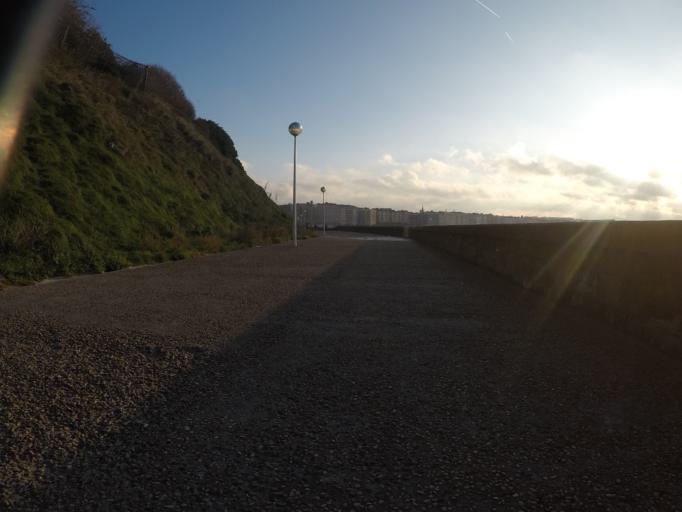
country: ES
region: Basque Country
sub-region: Provincia de Guipuzcoa
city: San Sebastian
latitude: 43.3306
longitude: -1.9717
